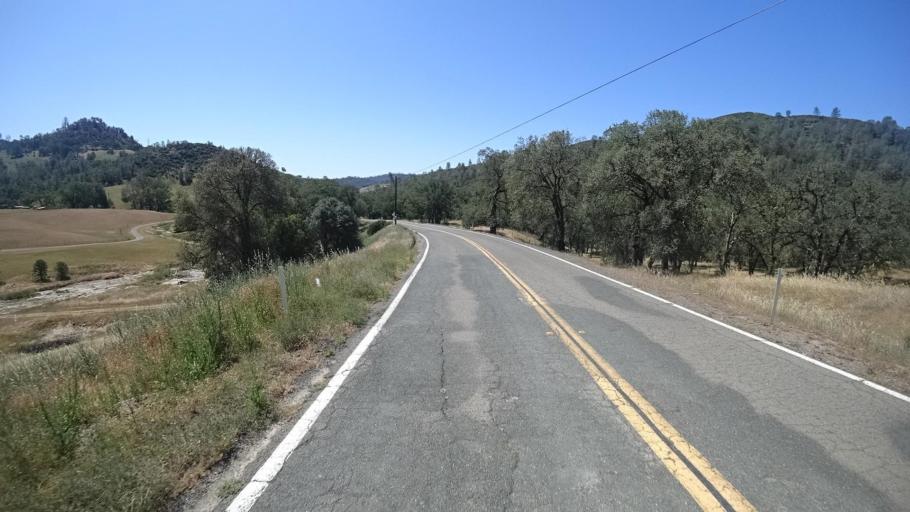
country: US
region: California
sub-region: Lake County
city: Lower Lake
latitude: 38.8878
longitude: -122.5348
